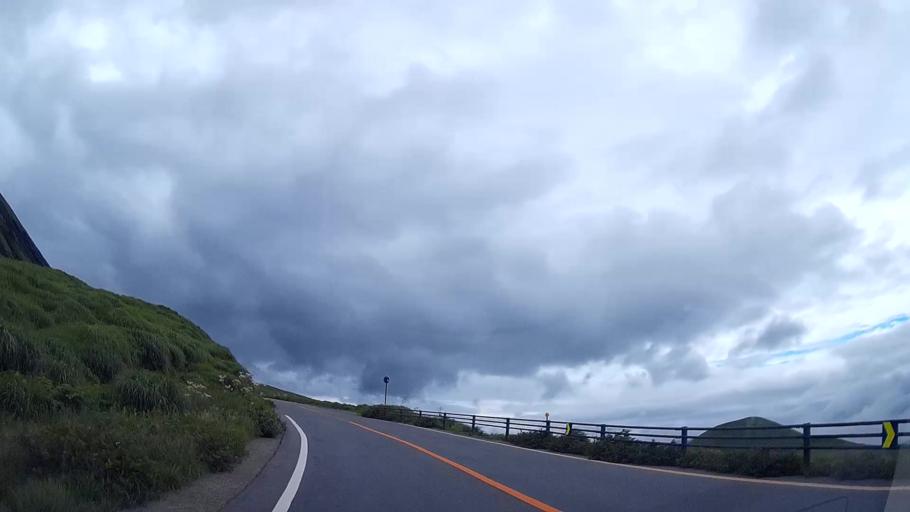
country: JP
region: Kumamoto
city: Aso
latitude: 32.9055
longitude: 131.0556
